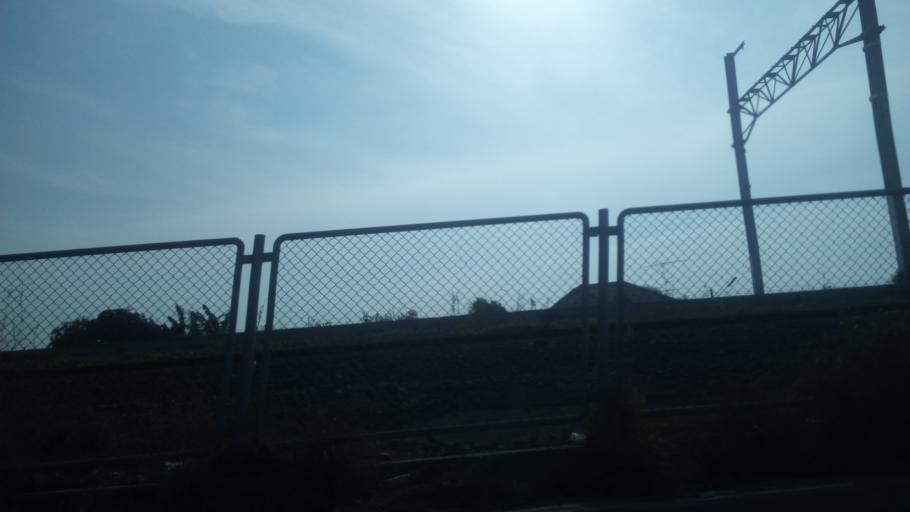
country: TH
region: Phra Nakhon Si Ayutthaya
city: Ban Bang Kadi Pathum Thani
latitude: 13.9787
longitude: 100.6036
